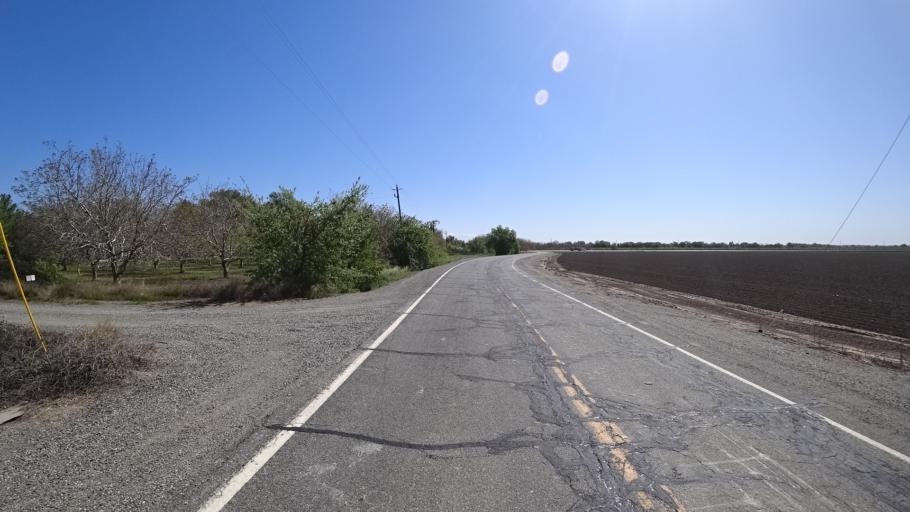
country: US
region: California
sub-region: Glenn County
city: Hamilton City
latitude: 39.7090
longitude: -122.0083
